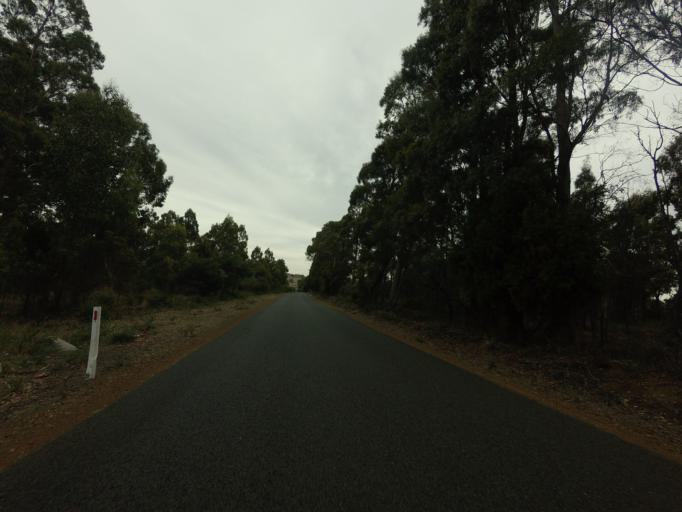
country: AU
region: Tasmania
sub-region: Sorell
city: Sorell
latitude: -42.5684
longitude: 147.5689
